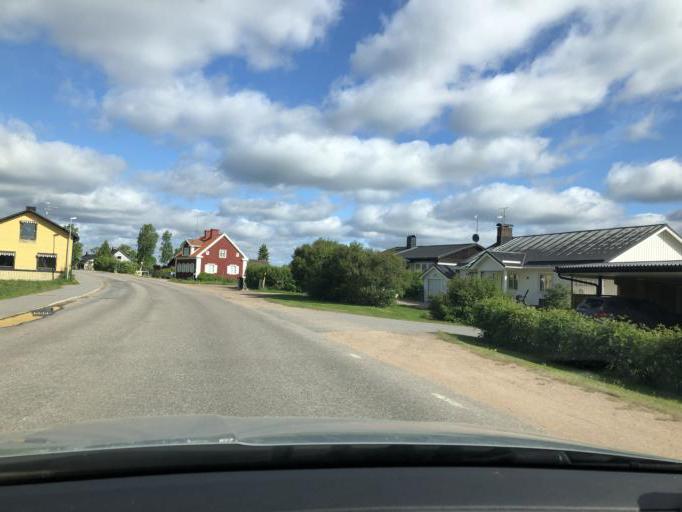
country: SE
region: Norrbotten
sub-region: Pajala Kommun
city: Pajala
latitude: 67.2152
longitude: 23.3662
